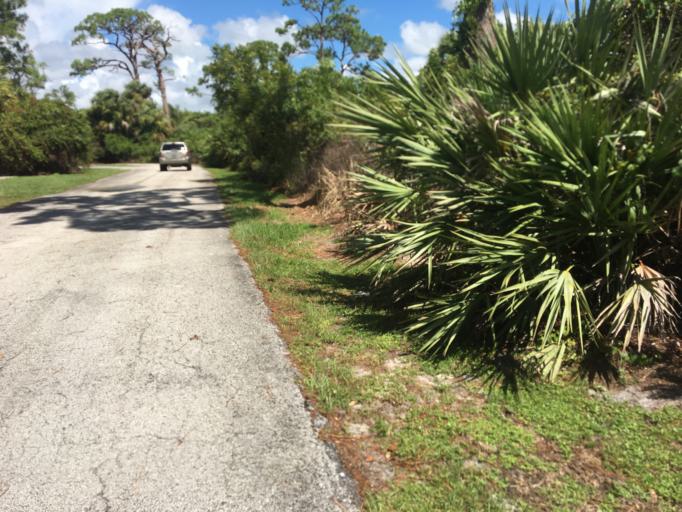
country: US
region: Florida
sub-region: Martin County
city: Stuart
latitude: 27.1879
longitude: -80.2705
